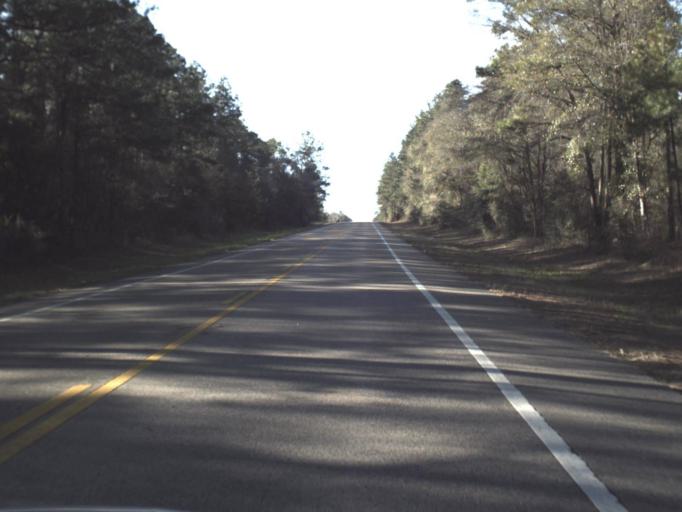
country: US
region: Florida
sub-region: Jackson County
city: Marianna
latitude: 30.6396
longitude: -85.1957
